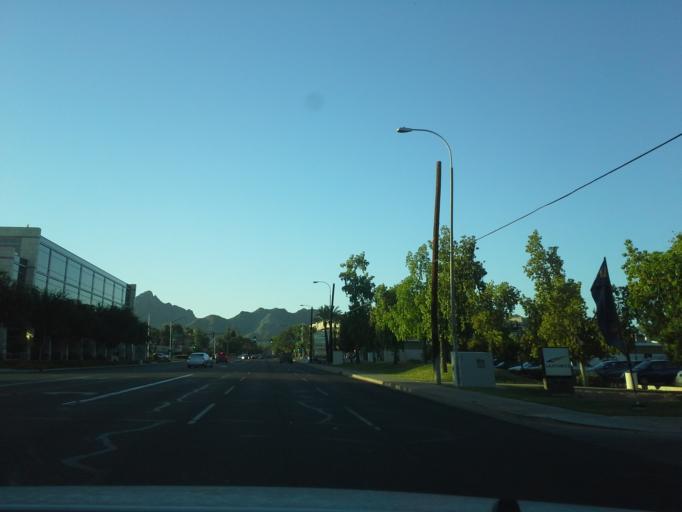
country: US
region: Arizona
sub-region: Maricopa County
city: Paradise Valley
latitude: 33.5082
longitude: -112.0130
